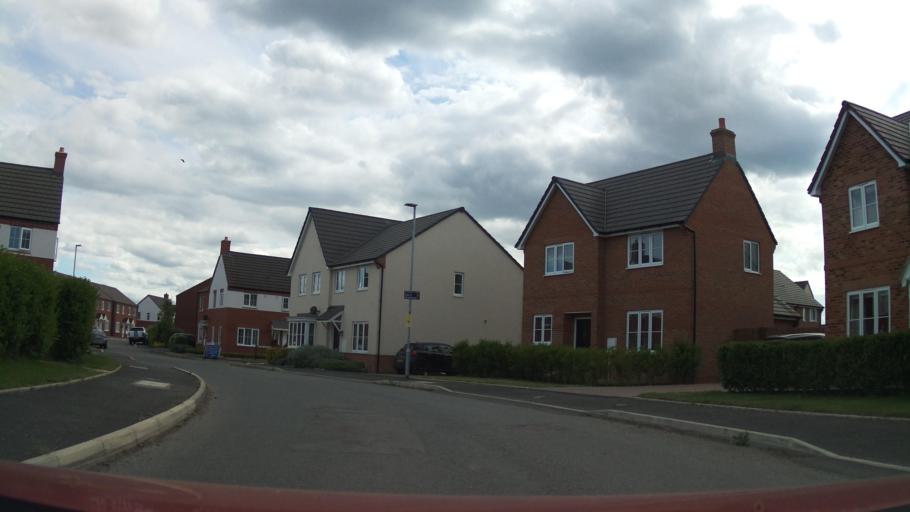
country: GB
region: England
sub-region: Worcestershire
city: Evesham
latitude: 52.0857
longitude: -1.9690
